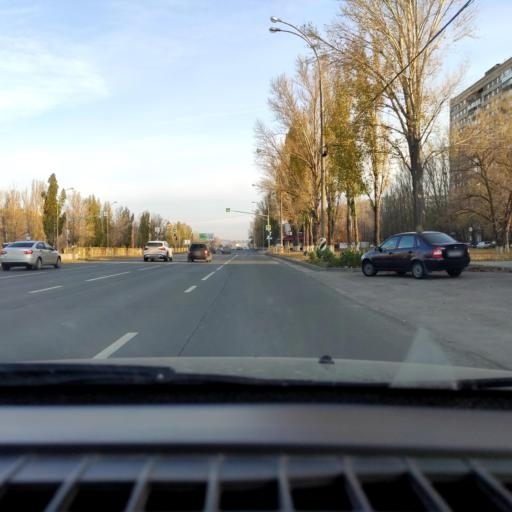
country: RU
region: Samara
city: Tol'yatti
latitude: 53.5238
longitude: 49.2806
